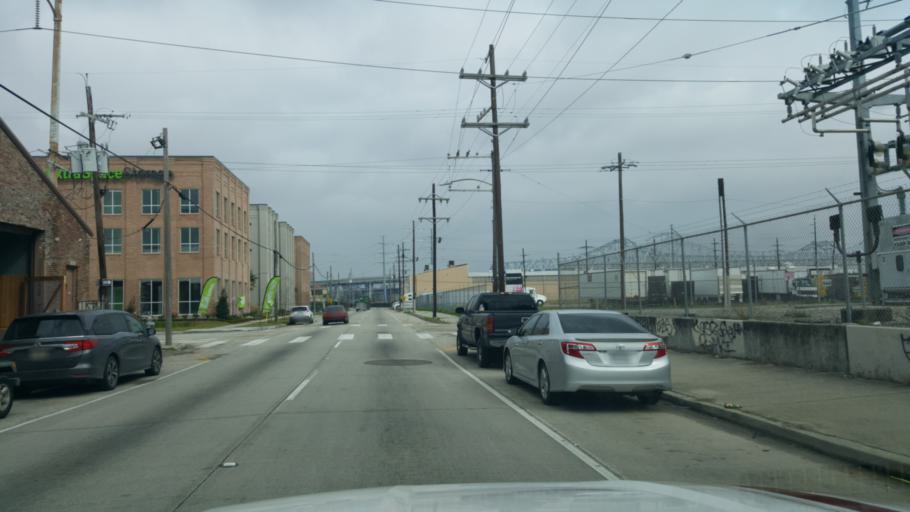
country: US
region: Louisiana
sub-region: Jefferson Parish
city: Gretna
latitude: 29.9295
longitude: -90.0666
